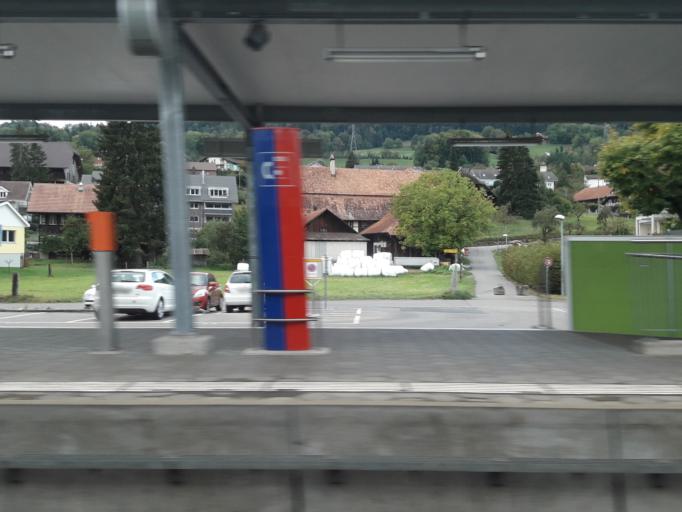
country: CH
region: Bern
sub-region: Bern-Mittelland District
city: Toffen
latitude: 46.8381
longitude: 7.5016
